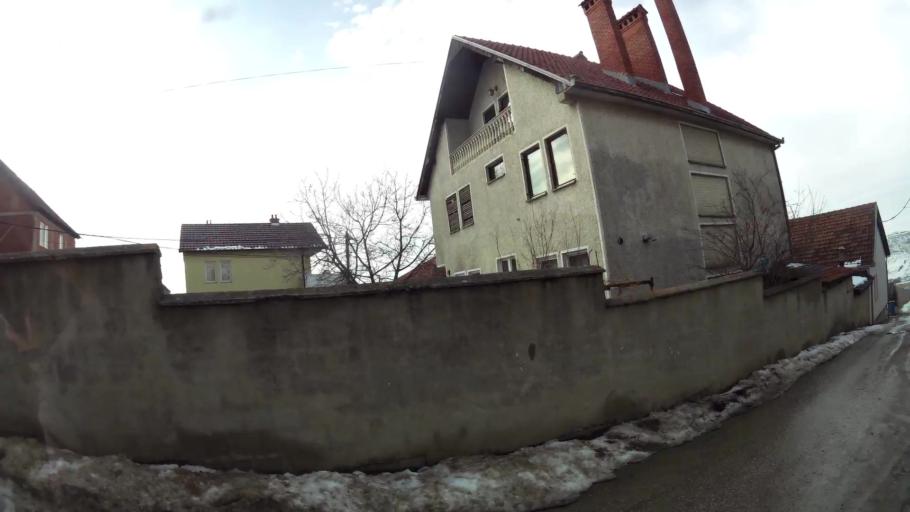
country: XK
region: Pristina
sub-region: Komuna e Prishtines
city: Pristina
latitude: 42.6849
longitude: 21.1541
